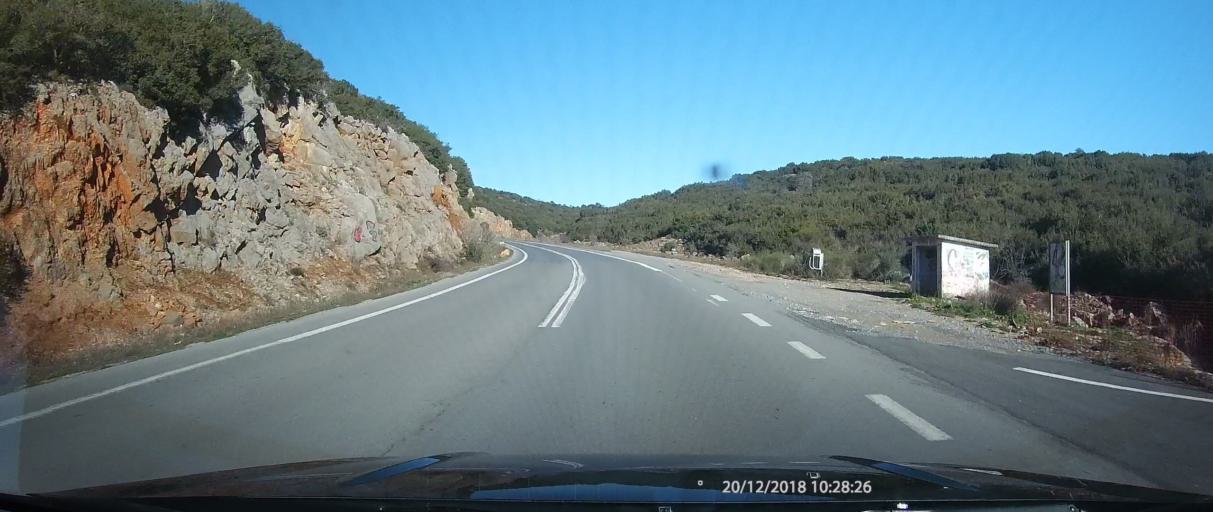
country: GR
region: Peloponnese
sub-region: Nomos Lakonias
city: Kariai
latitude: 37.2619
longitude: 22.4361
